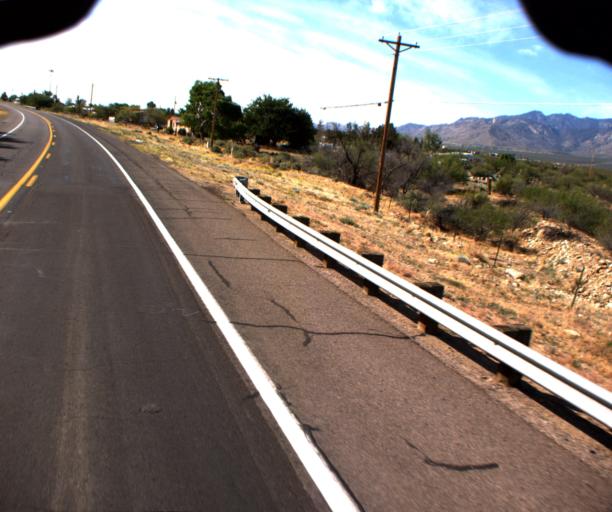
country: US
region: Arizona
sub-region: Graham County
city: Swift Trail Junction
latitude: 32.7342
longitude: -109.7161
